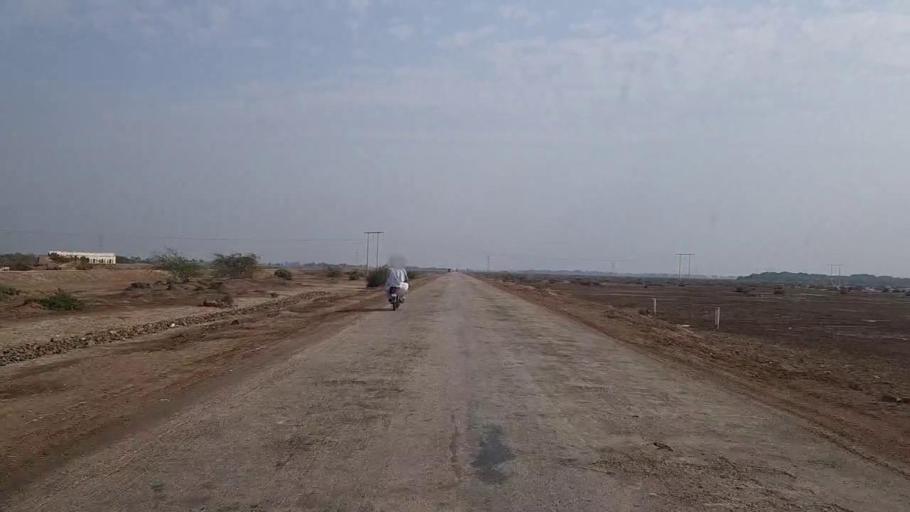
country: PK
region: Sindh
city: Mirpur Khas
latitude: 25.4250
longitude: 69.0202
